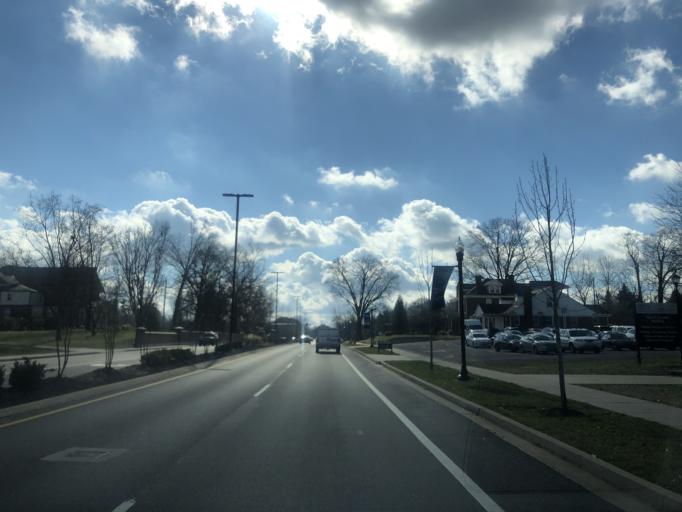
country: US
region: Tennessee
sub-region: Rutherford County
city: Murfreesboro
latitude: 35.8461
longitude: -86.3718
